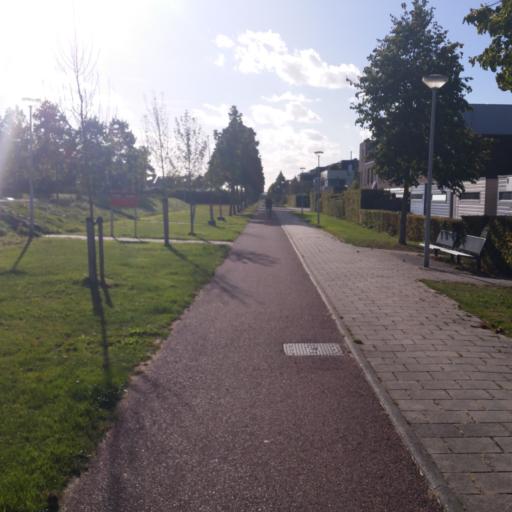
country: NL
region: Utrecht
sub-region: Gemeente IJsselstein
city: IJsselstein
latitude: 52.0141
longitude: 5.0352
